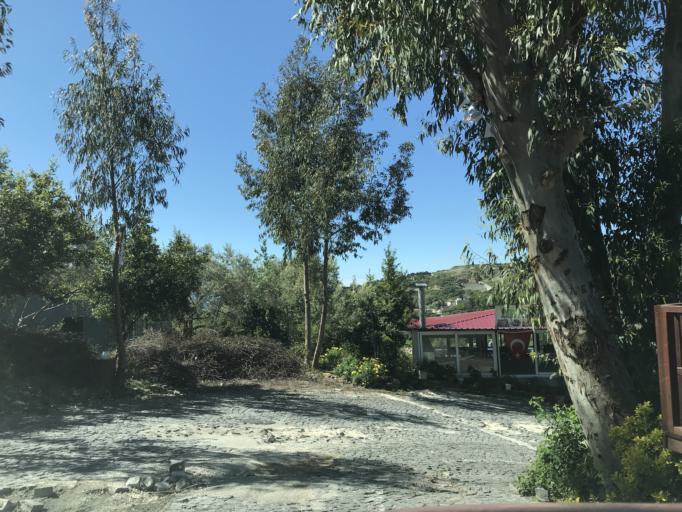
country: TR
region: Hatay
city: Samandag
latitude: 36.1322
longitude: 35.9764
